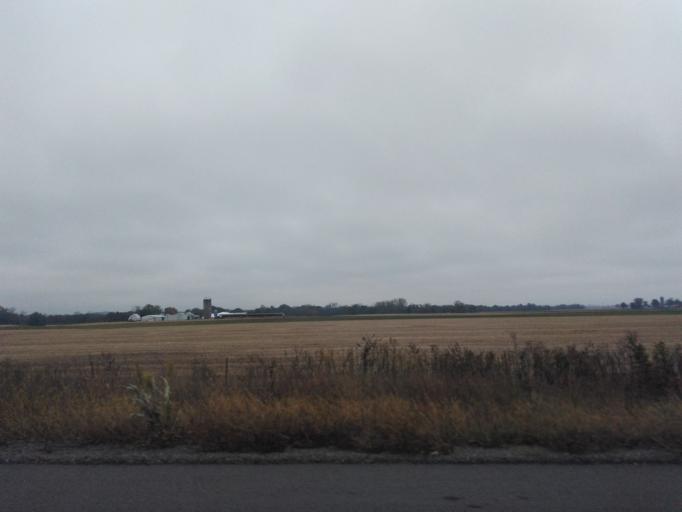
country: US
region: Illinois
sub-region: Madison County
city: Highland
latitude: 38.7865
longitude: -89.6374
